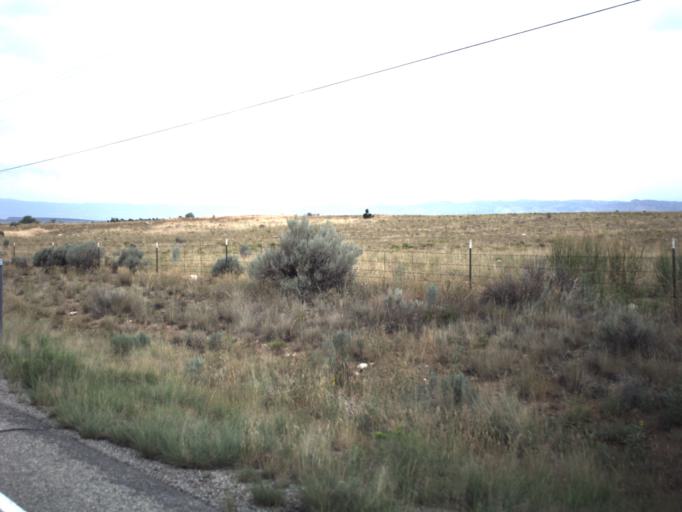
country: US
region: Utah
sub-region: Carbon County
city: East Carbon City
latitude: 39.5369
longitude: -110.4566
